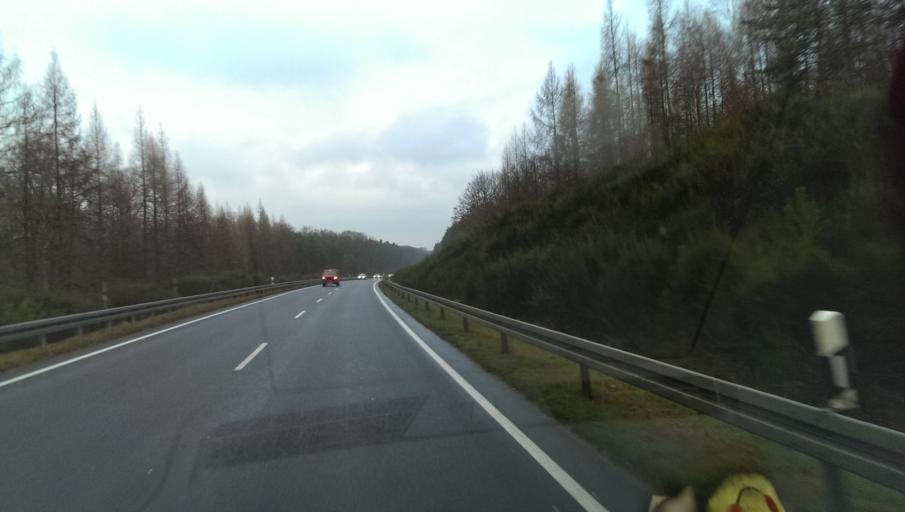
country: DE
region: Saxony
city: Moritzburg
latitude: 51.1555
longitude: 13.6405
